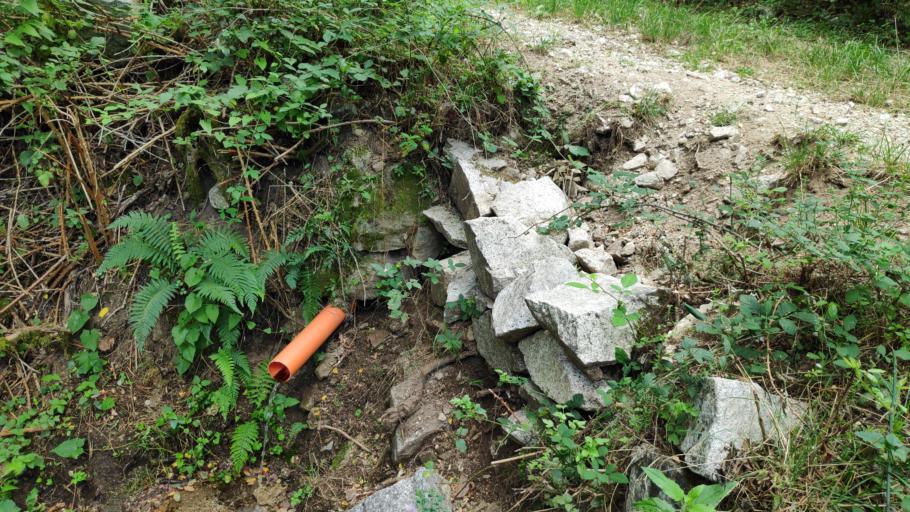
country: IT
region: Calabria
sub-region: Provincia di Reggio Calabria
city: Pazzano
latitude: 38.4766
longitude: 16.4092
